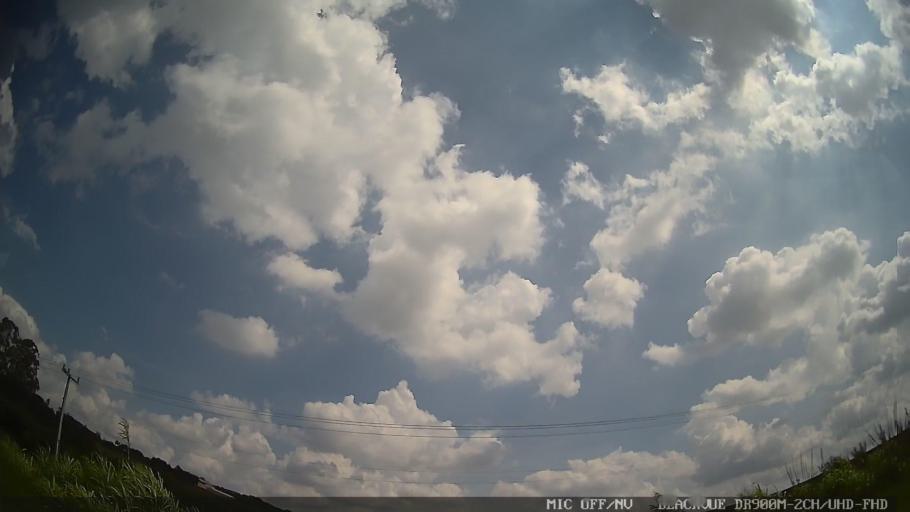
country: BR
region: Sao Paulo
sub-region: Braganca Paulista
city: Braganca Paulista
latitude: -22.9446
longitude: -46.6690
